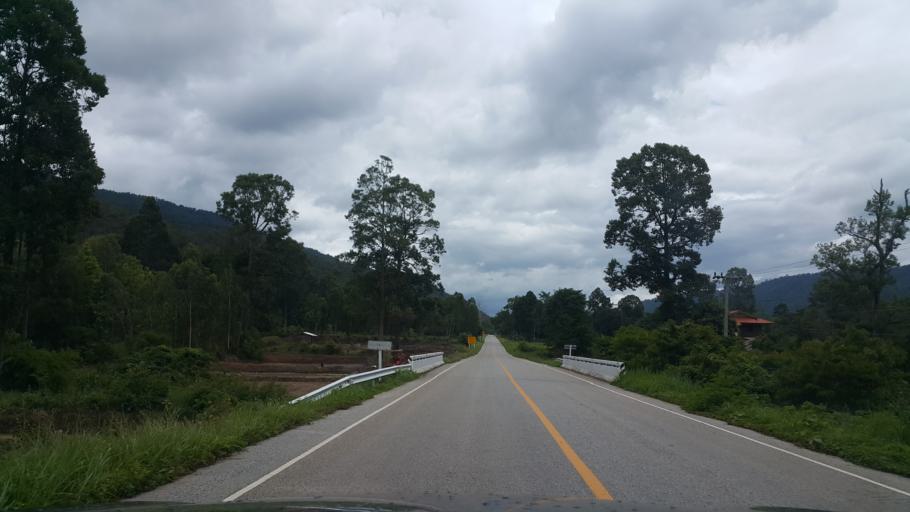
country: TH
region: Phitsanulok
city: Chat Trakan
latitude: 17.3319
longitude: 100.7031
